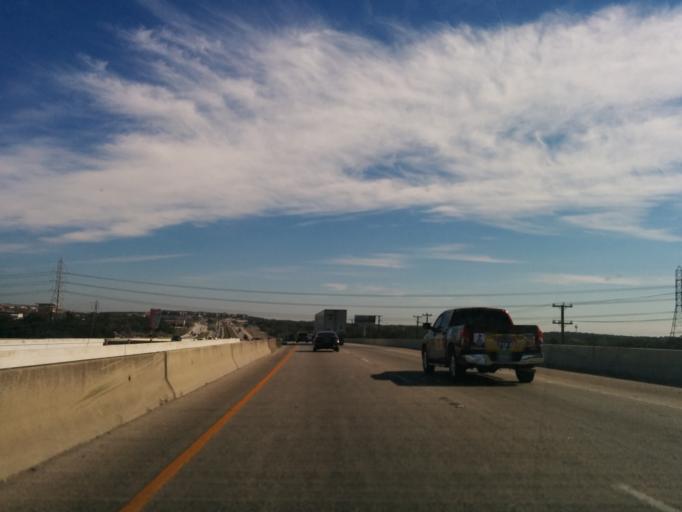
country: US
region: Texas
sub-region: Bexar County
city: Shavano Park
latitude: 29.5935
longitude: -98.5774
